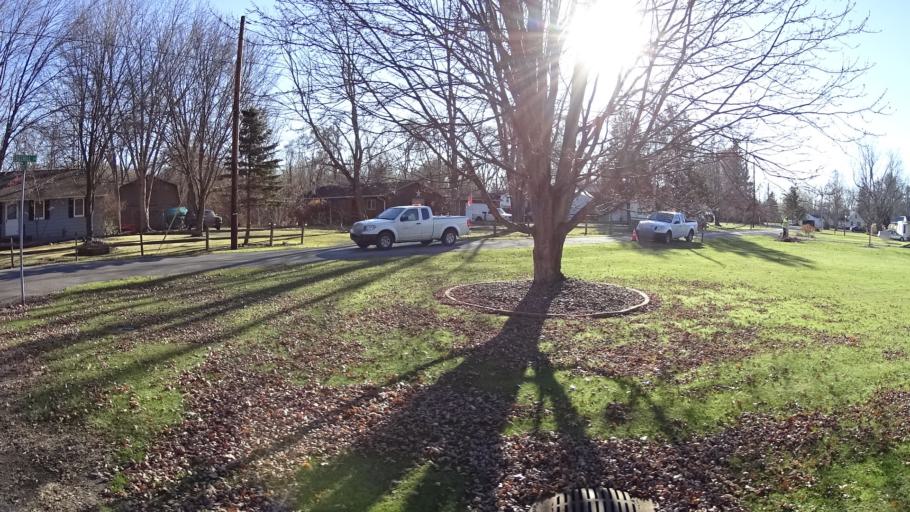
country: US
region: Ohio
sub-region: Lorain County
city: Elyria
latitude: 41.3262
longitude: -82.1281
